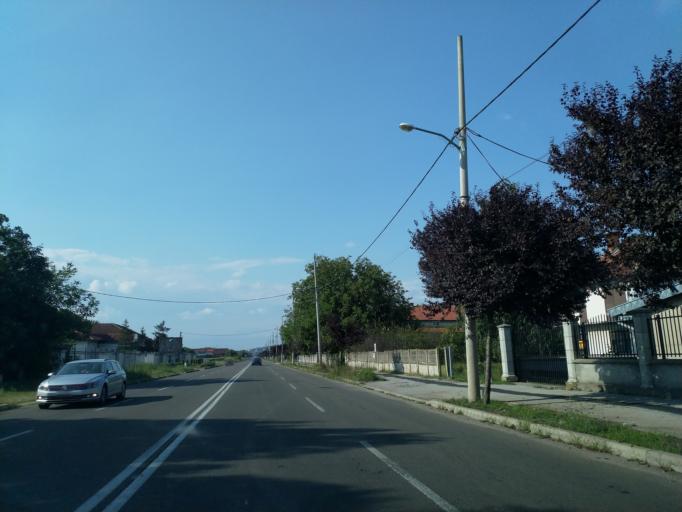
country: RS
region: Central Serbia
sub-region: Pomoravski Okrug
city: Paracin
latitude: 43.8365
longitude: 21.4159
